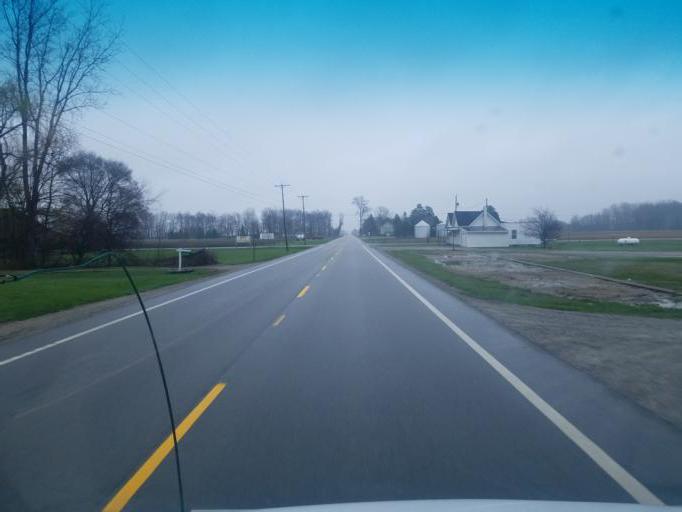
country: US
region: Ohio
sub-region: Wood County
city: Weston
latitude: 41.3721
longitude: -83.7974
